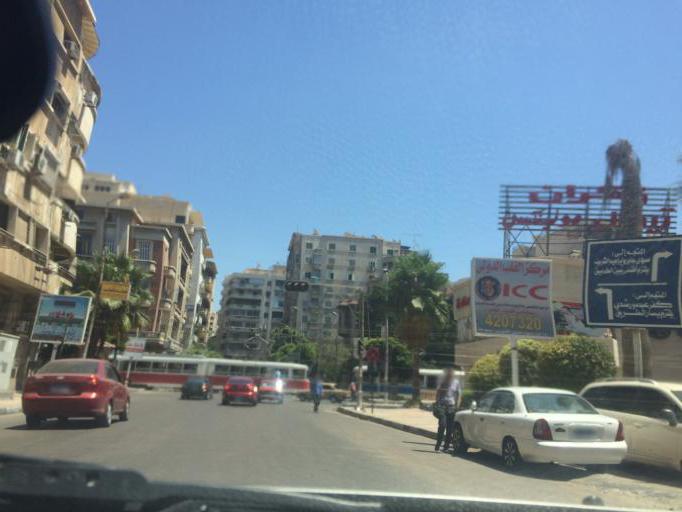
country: EG
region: Alexandria
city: Alexandria
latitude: 31.2285
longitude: 29.9498
